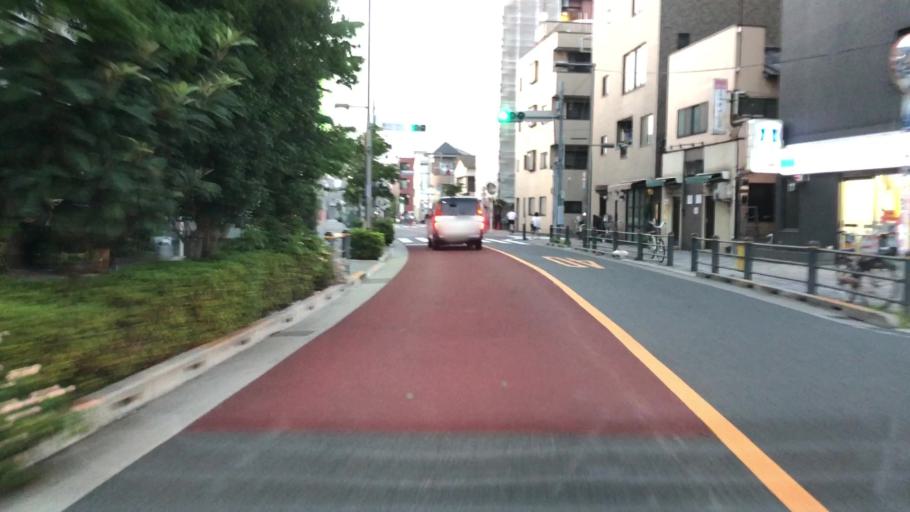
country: JP
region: Saitama
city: Soka
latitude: 35.7405
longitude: 139.7740
